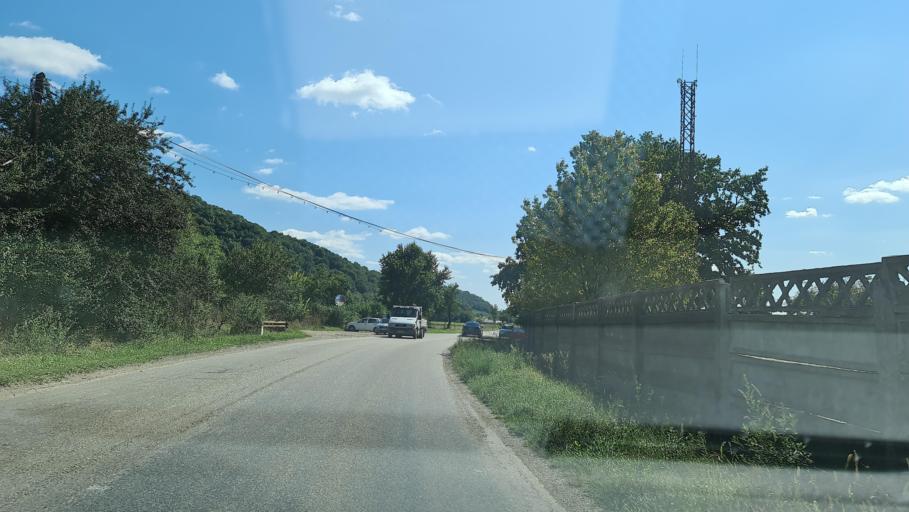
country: RO
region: Bacau
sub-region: Comuna Scorteni
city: Scorteni
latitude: 46.5178
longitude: 26.6706
